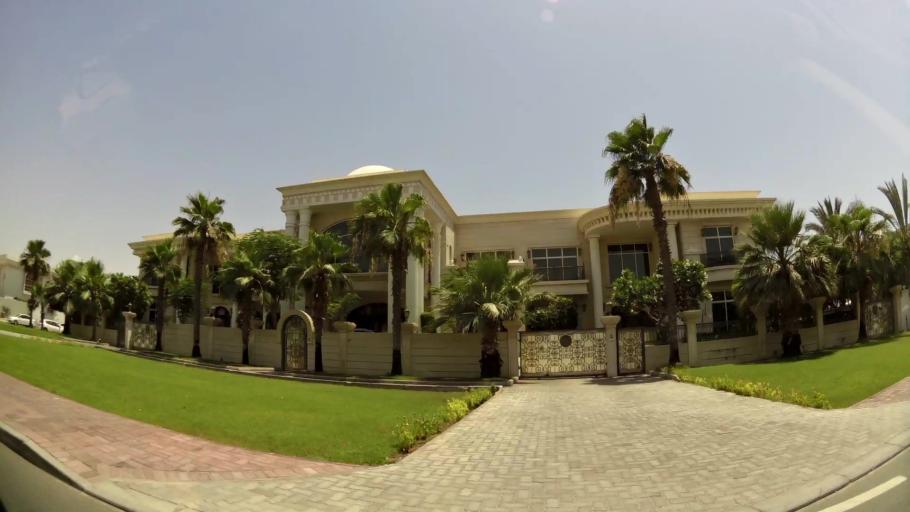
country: AE
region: Dubai
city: Dubai
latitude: 25.1846
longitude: 55.2326
